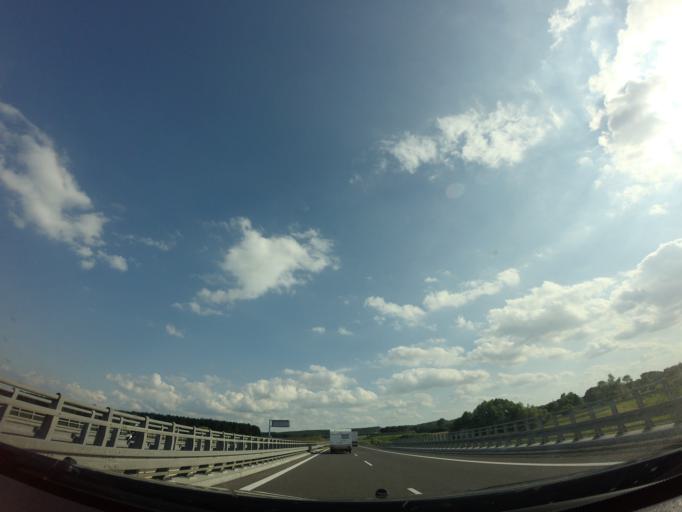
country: PL
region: Lubusz
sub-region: Powiat swiebodzinski
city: Swiebodzin
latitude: 52.3404
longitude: 15.5575
